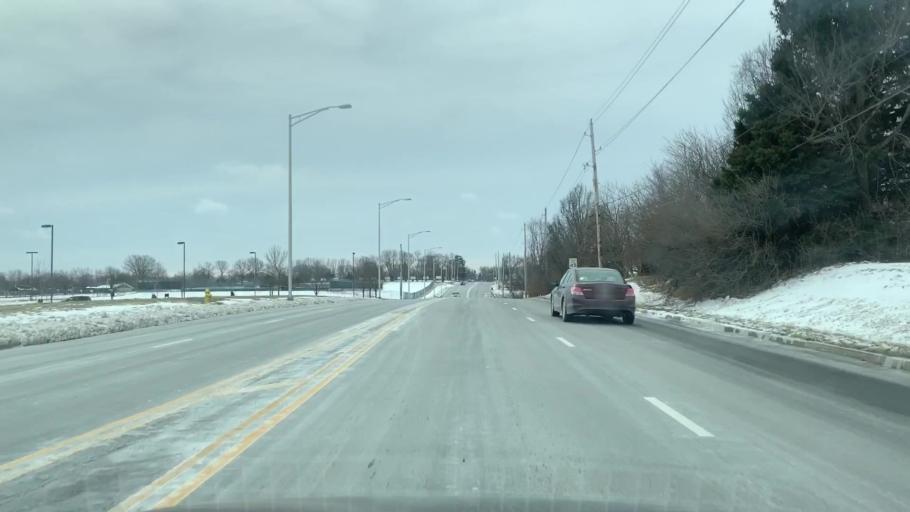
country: US
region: Missouri
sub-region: Jackson County
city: Lees Summit
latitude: 38.9296
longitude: -94.3797
